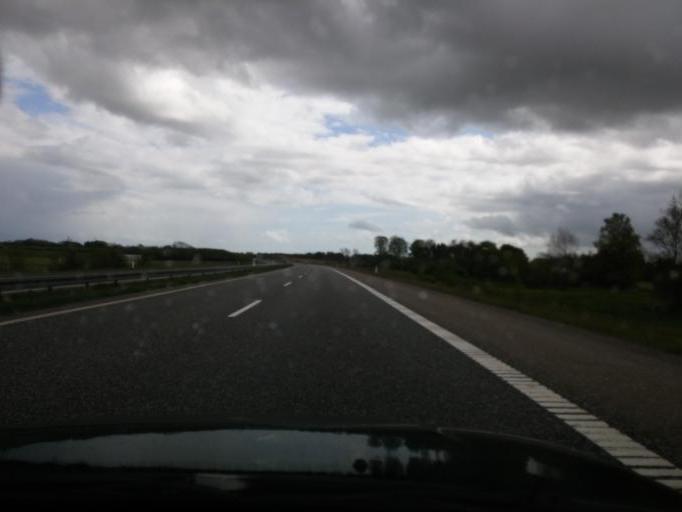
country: DK
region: South Denmark
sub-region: Faaborg-Midtfyn Kommune
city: Arslev
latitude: 55.2922
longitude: 10.4414
